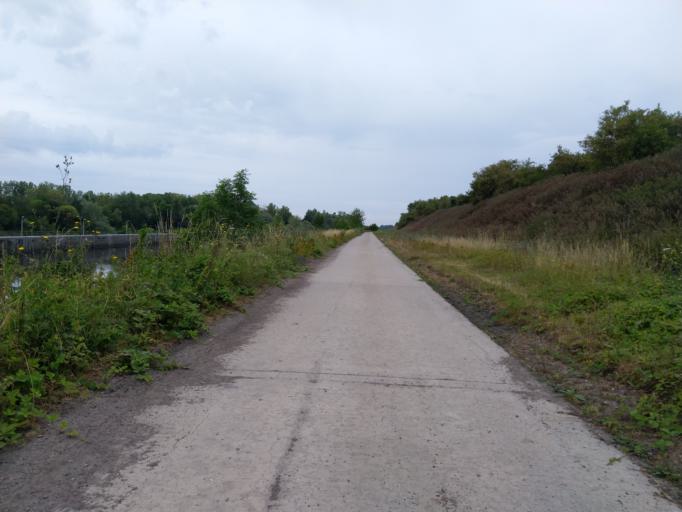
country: BE
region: Wallonia
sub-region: Province du Hainaut
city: Hensies
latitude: 50.4504
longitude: 3.6686
